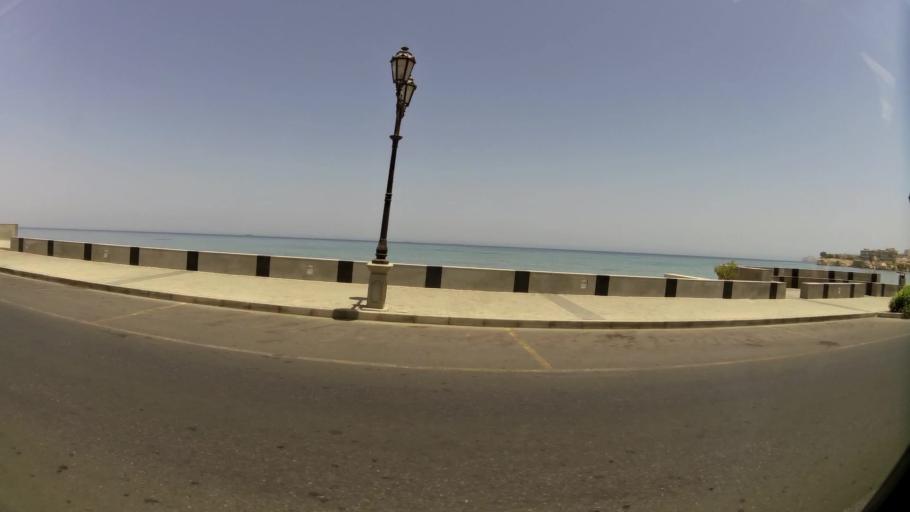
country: OM
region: Muhafazat Masqat
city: Bawshar
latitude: 23.6241
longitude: 58.4776
